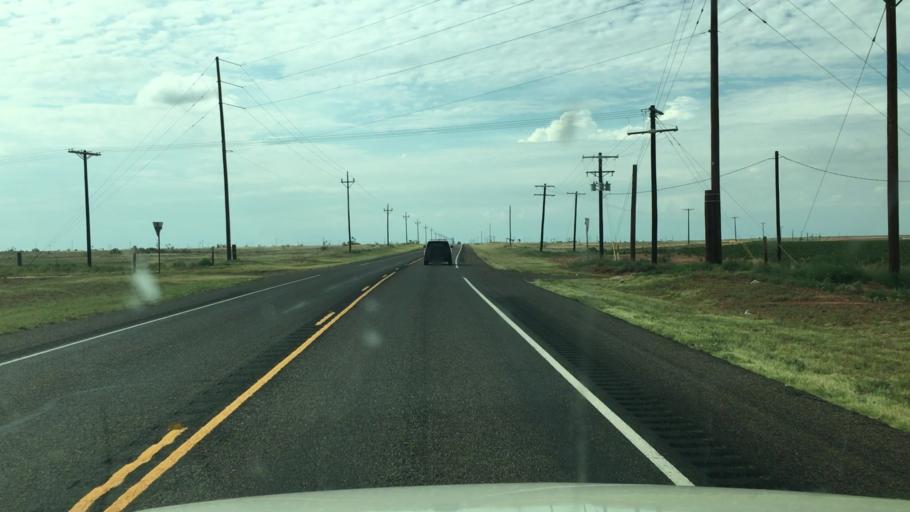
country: US
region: Texas
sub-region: Dawson County
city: Lamesa
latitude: 32.8893
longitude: -102.0890
